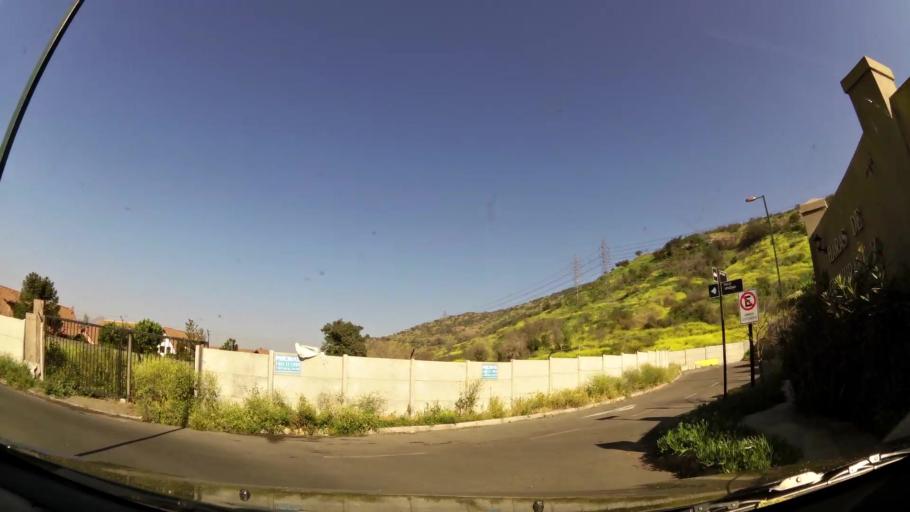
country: CL
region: Santiago Metropolitan
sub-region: Provincia de Chacabuco
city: Chicureo Abajo
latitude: -33.3464
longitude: -70.6787
